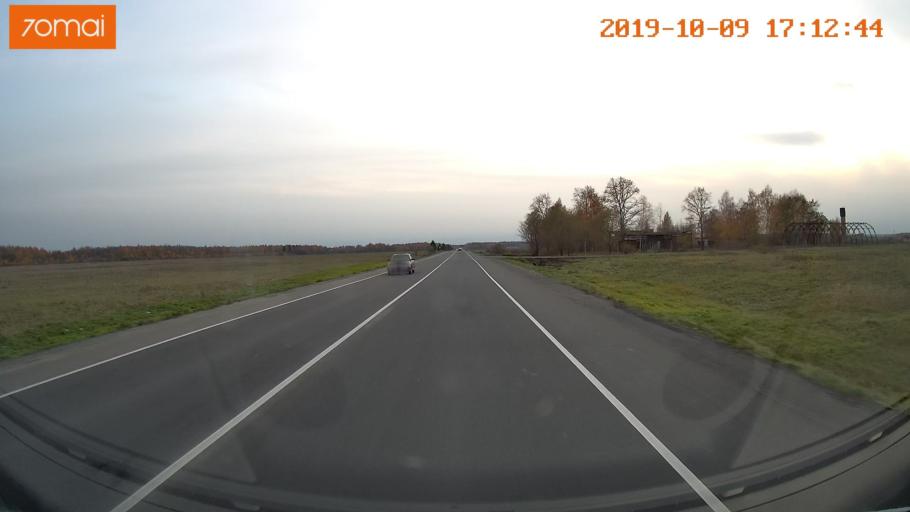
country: RU
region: Ivanovo
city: Privolzhsk
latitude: 57.3245
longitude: 41.2365
